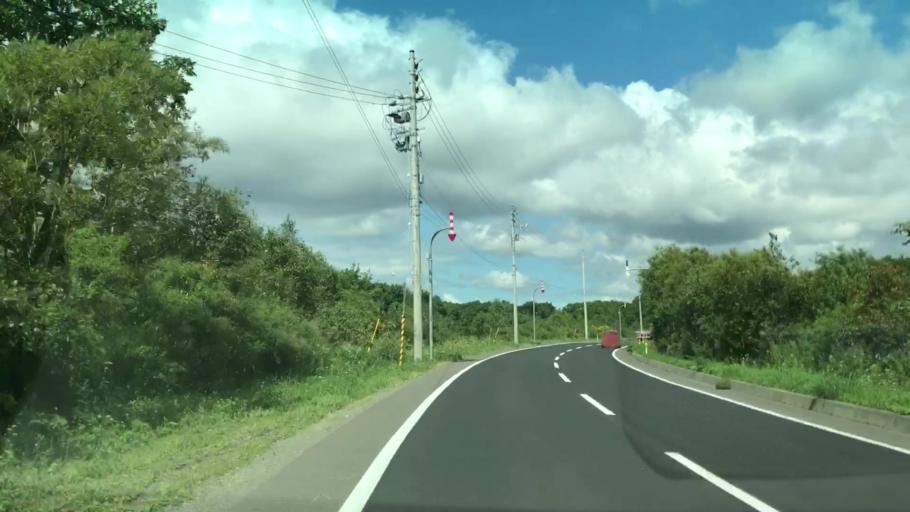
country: JP
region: Hokkaido
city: Chitose
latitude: 42.7637
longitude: 141.6651
